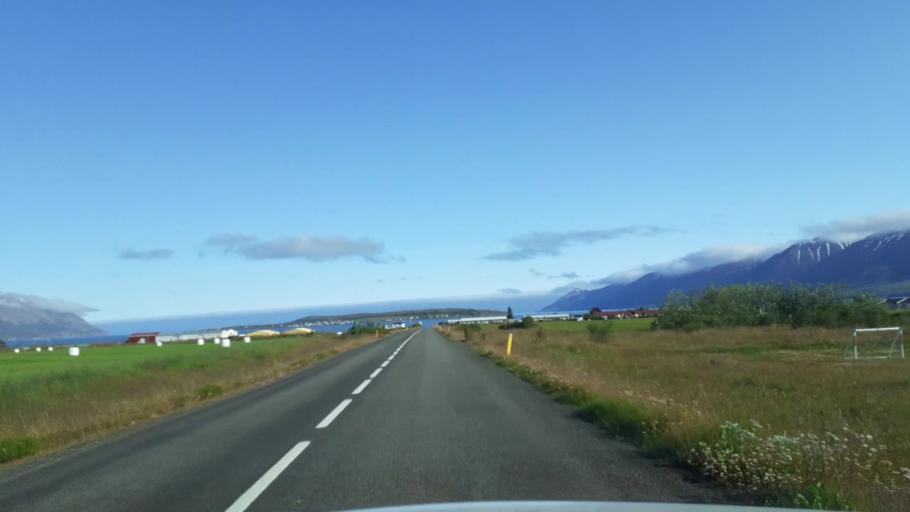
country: IS
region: Northeast
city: Dalvik
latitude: 65.9399
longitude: -18.3535
